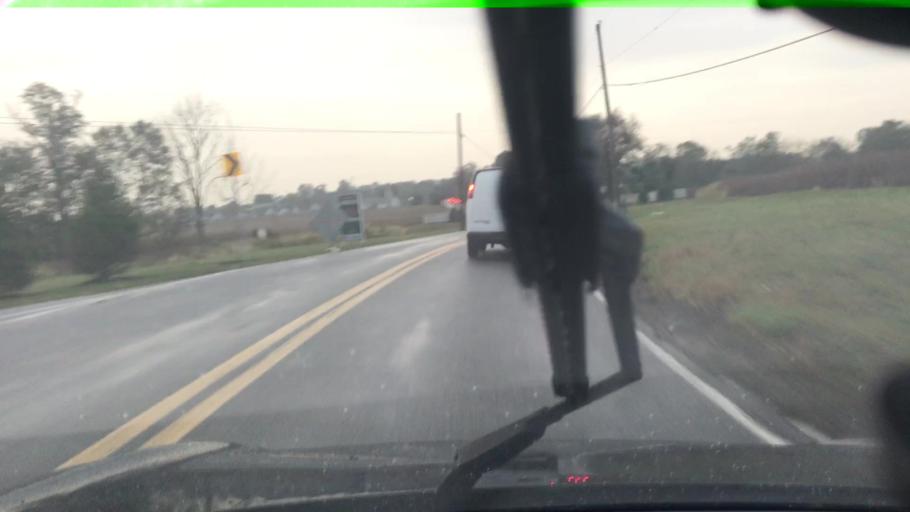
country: US
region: Pennsylvania
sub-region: Cumberland County
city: Shiremanstown
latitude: 40.1941
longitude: -76.9406
